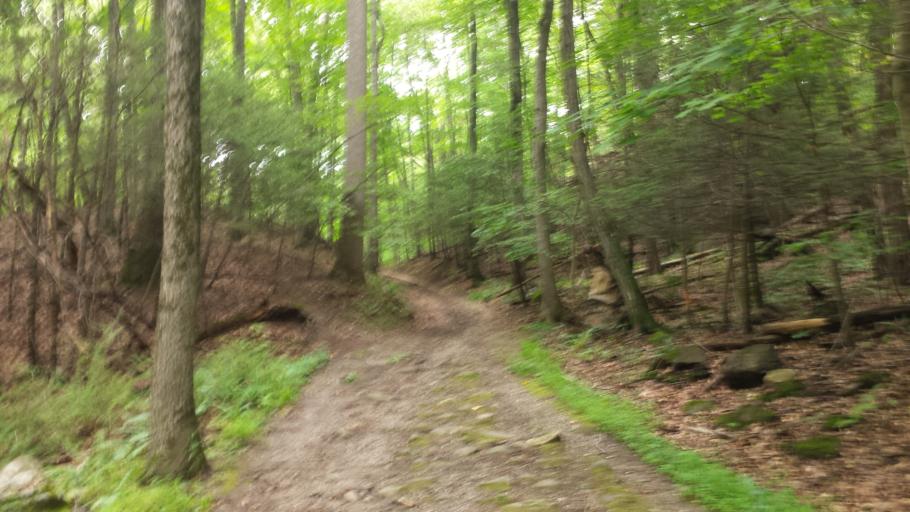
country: US
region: New York
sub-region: Westchester County
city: Peekskill
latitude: 41.2726
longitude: -73.9196
